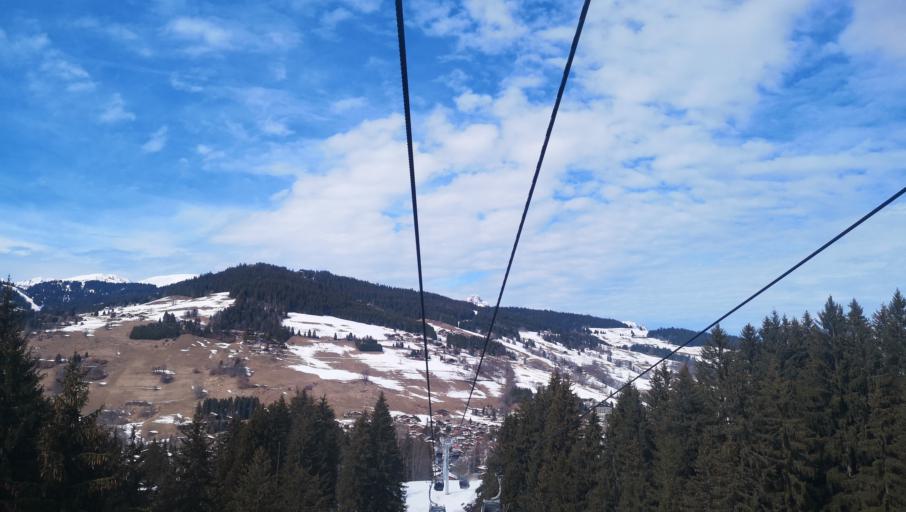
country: FR
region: Rhone-Alpes
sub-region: Departement de la Haute-Savoie
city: Megeve
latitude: 45.8510
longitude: 6.6213
